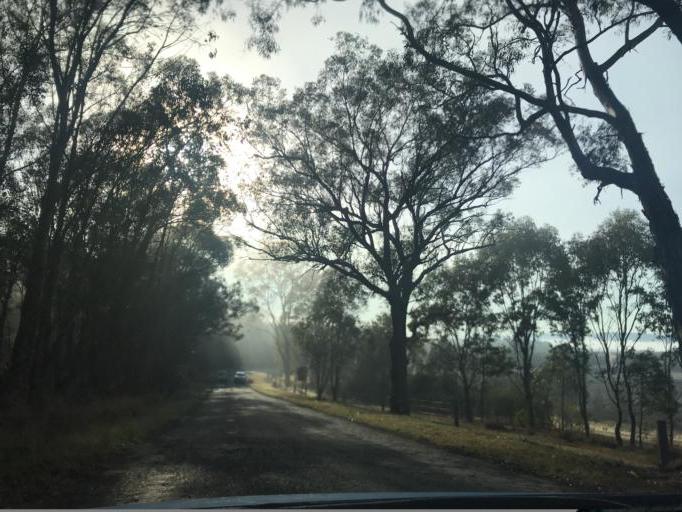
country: AU
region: New South Wales
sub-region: Cessnock
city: Cessnock
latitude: -32.9069
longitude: 151.2858
